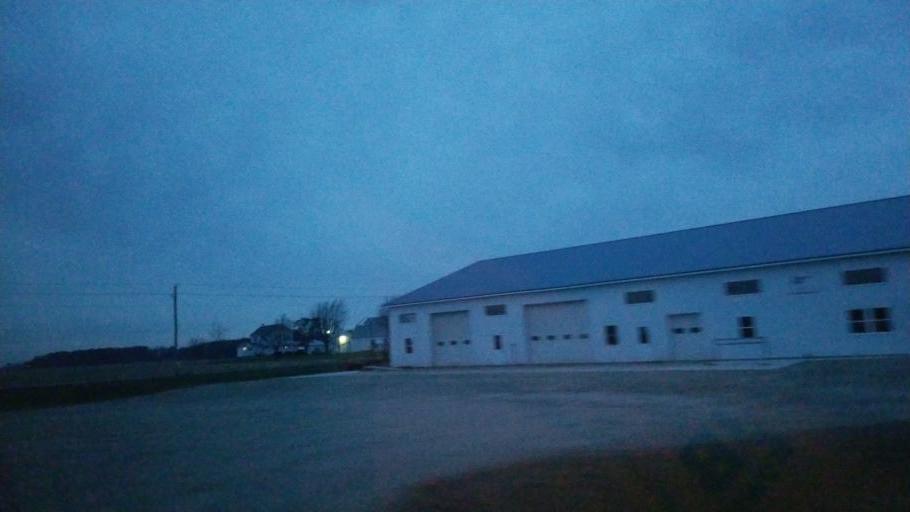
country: US
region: Indiana
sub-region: Adams County
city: Berne
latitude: 40.6934
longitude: -84.9935
